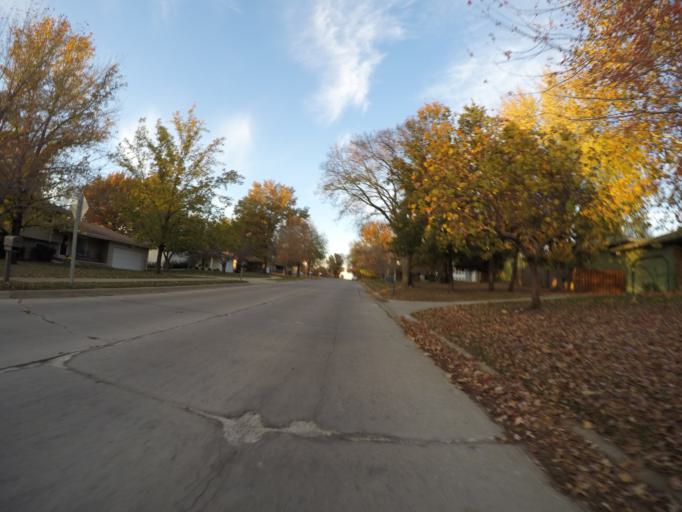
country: US
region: Kansas
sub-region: Riley County
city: Manhattan
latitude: 39.1940
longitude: -96.6167
